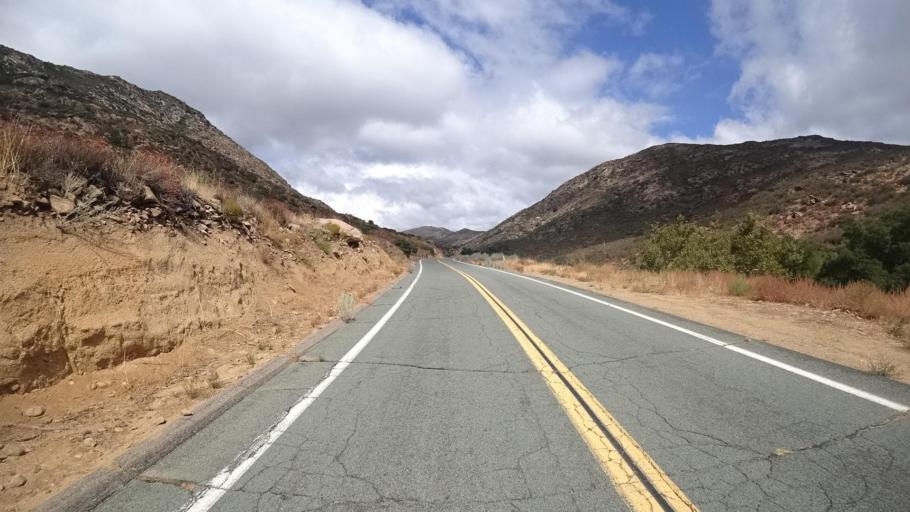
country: US
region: California
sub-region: San Diego County
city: Pine Valley
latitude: 32.7656
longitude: -116.4517
